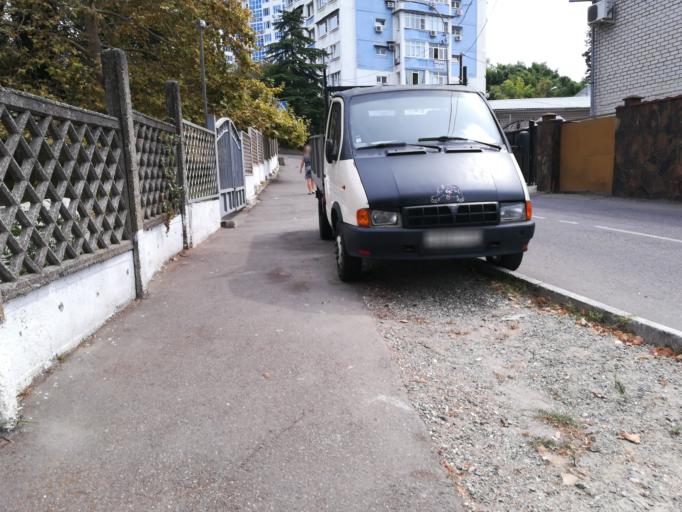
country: RU
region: Krasnodarskiy
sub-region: Sochi City
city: Sochi
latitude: 43.5912
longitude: 39.7368
